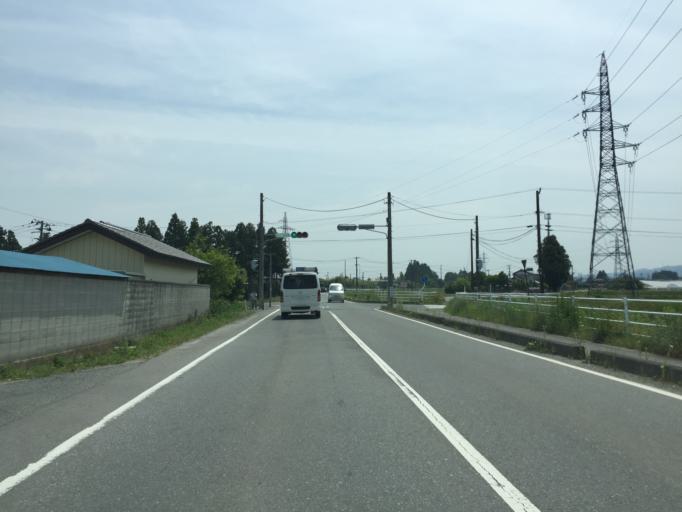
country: JP
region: Fukushima
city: Namie
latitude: 37.6285
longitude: 140.9362
